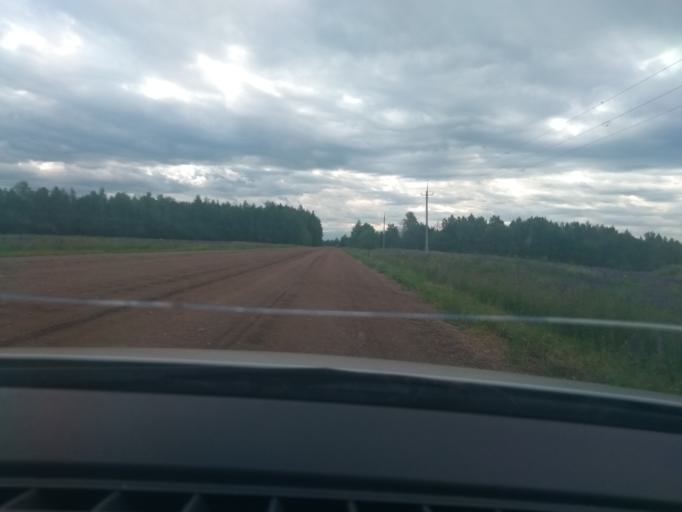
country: RU
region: Perm
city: Sylva
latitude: 57.8183
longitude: 56.7204
